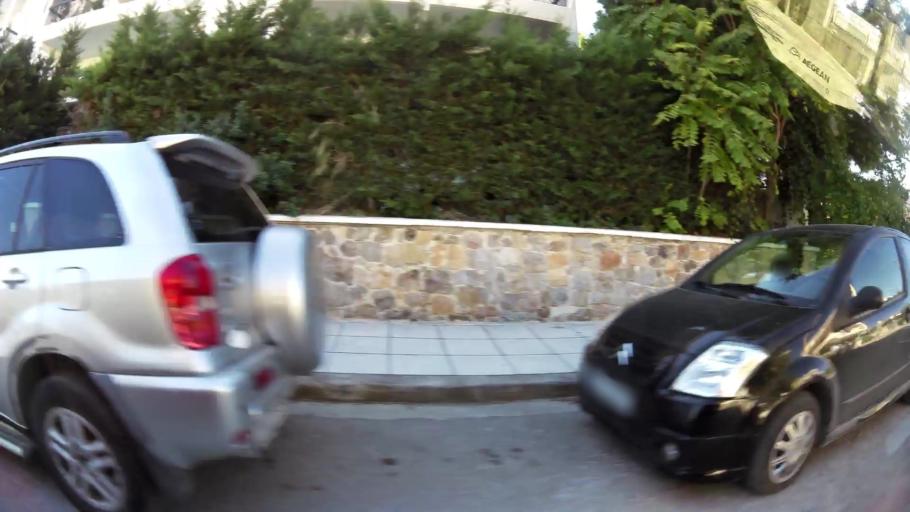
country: GR
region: Attica
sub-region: Nomarchia Anatolikis Attikis
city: Paiania
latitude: 37.9574
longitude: 23.8585
